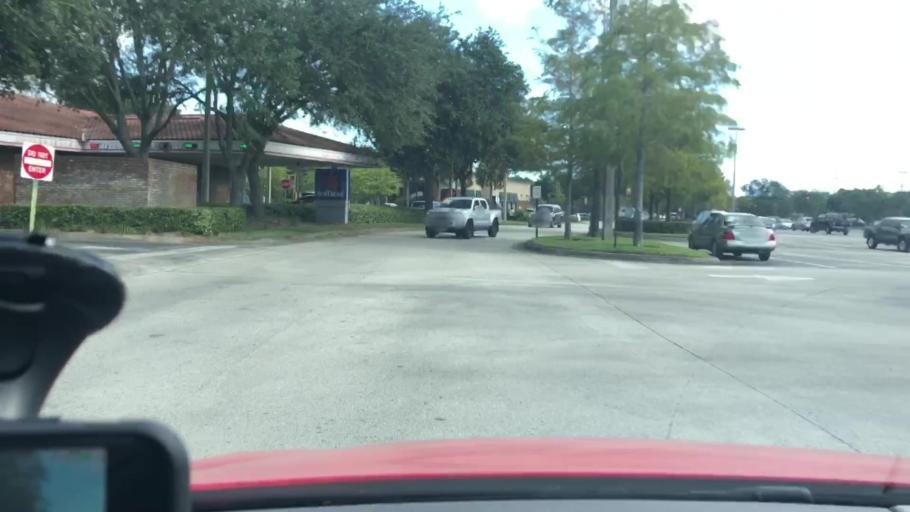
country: US
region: Florida
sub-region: Volusia County
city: Ormond Beach
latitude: 29.2571
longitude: -81.1117
